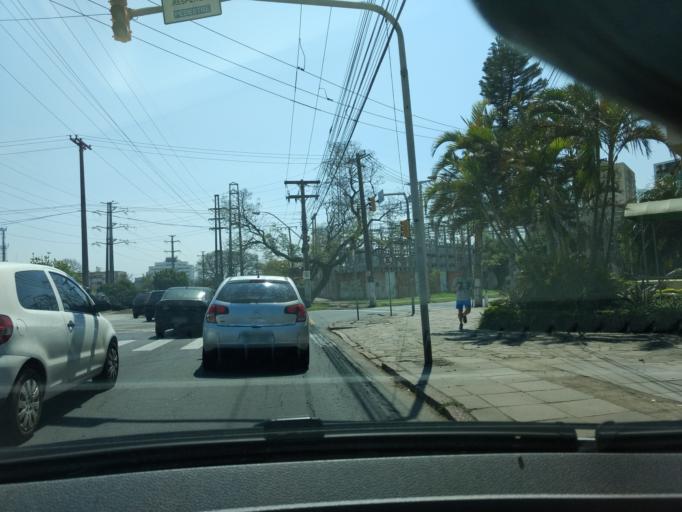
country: BR
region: Rio Grande do Sul
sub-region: Porto Alegre
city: Porto Alegre
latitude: -30.0484
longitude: -51.1961
